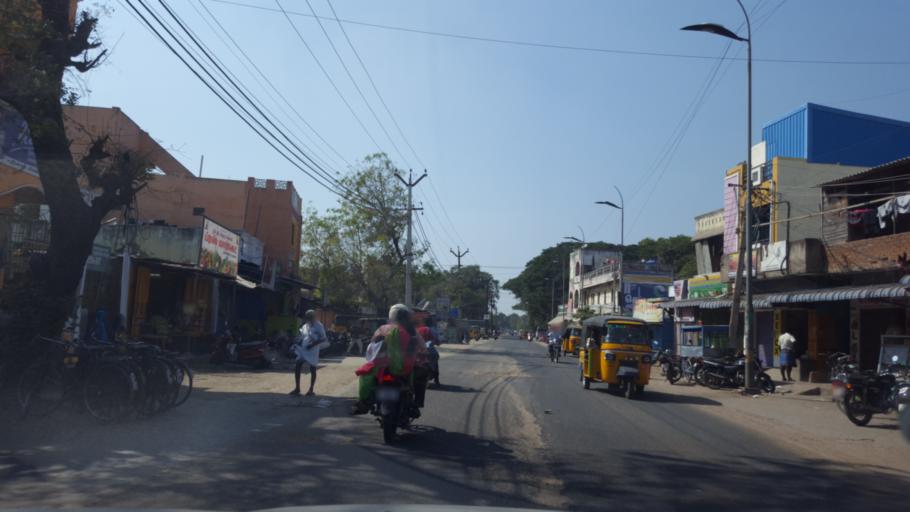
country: IN
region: Tamil Nadu
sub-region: Kancheepuram
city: Kanchipuram
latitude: 12.8513
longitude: 79.6913
